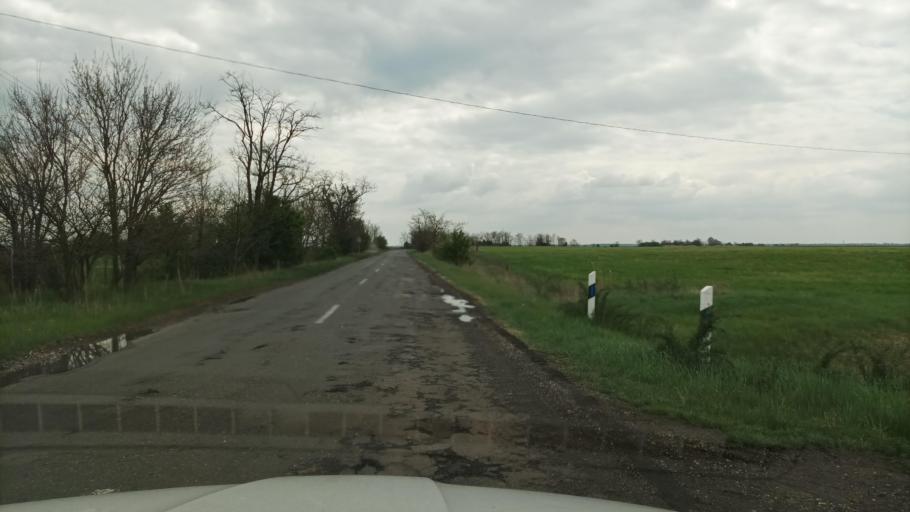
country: HU
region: Pest
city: Abony
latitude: 47.1693
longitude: 19.9781
